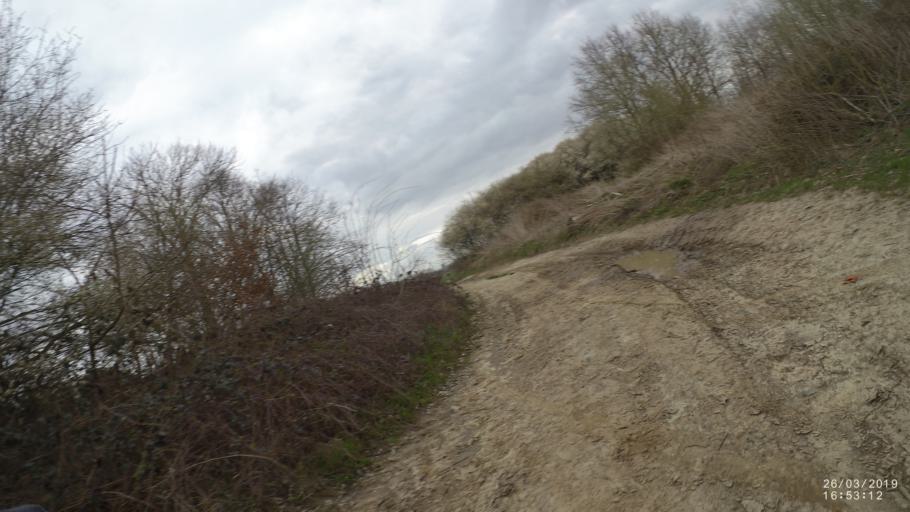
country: BE
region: Flanders
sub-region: Provincie Vlaams-Brabant
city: Bertem
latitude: 50.8409
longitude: 4.6300
